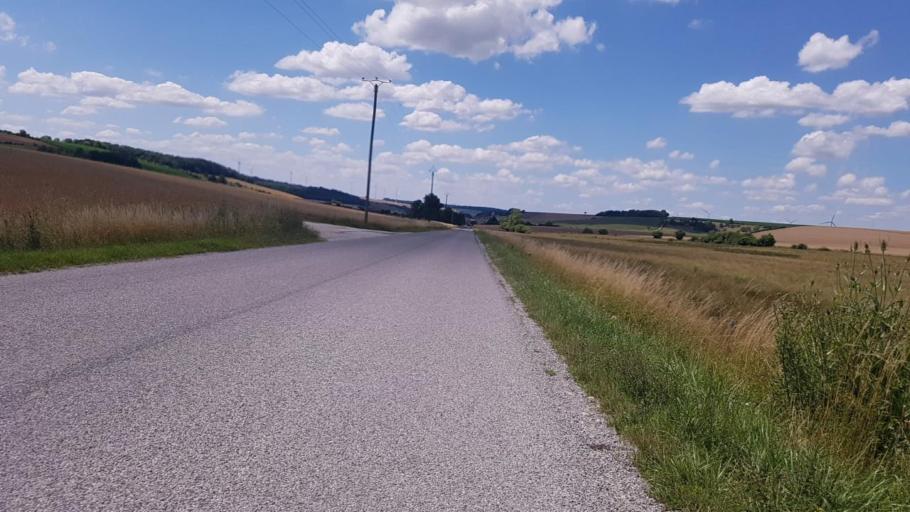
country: FR
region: Lorraine
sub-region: Departement de la Meuse
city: Vacon
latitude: 48.6513
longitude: 5.5267
